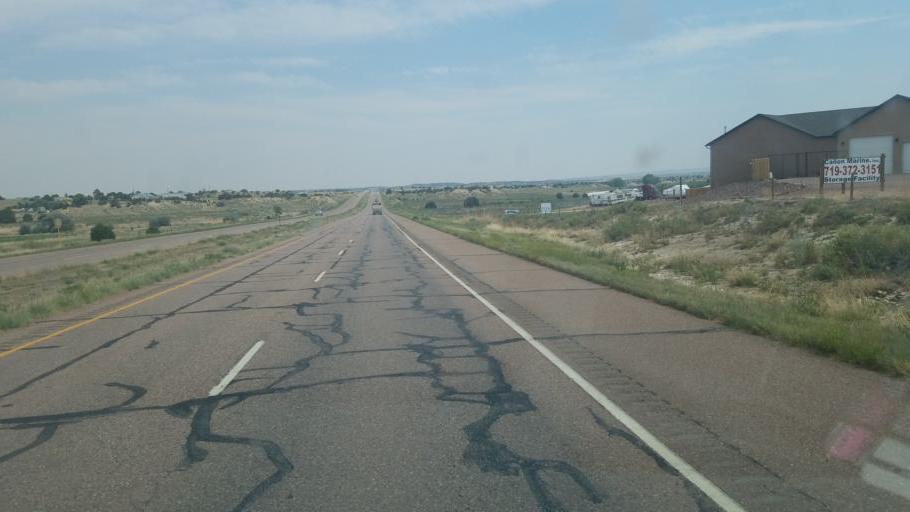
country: US
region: Colorado
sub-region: Fremont County
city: Penrose
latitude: 38.3998
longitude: -104.9798
